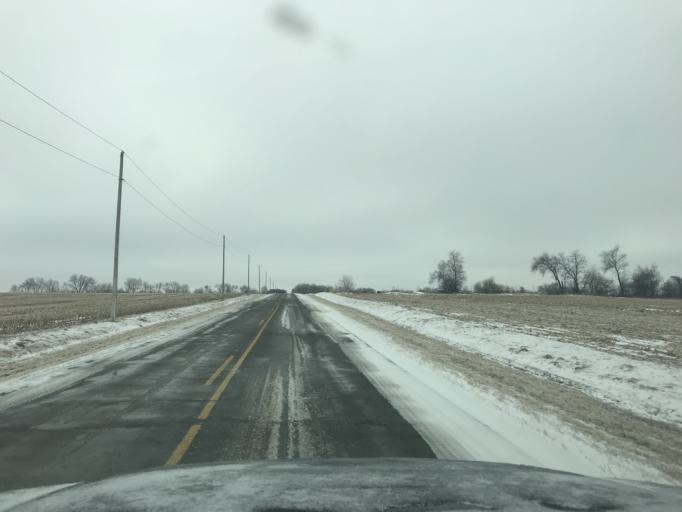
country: US
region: Wisconsin
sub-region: Dane County
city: Cottage Grove
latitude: 43.1021
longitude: -89.2296
